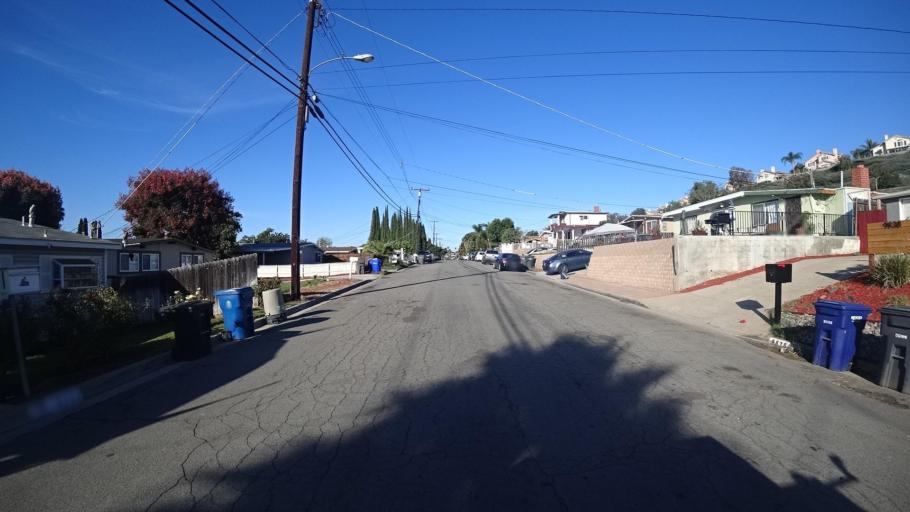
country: US
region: California
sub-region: San Diego County
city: La Presa
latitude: 32.7107
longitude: -116.9854
